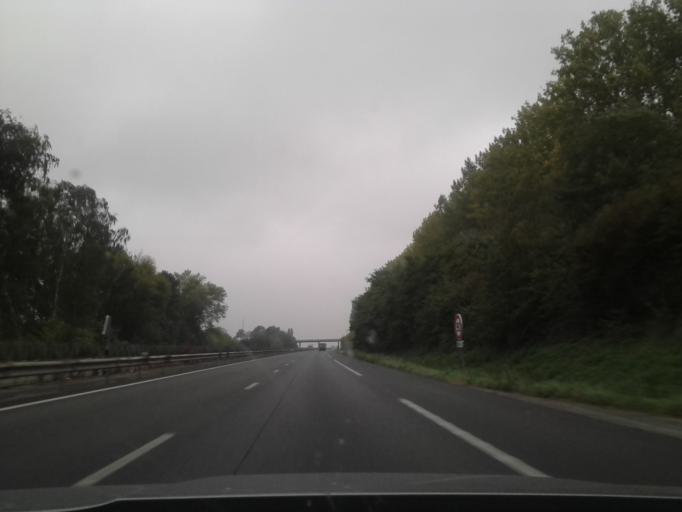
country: FR
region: Nord-Pas-de-Calais
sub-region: Departement du Nord
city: Neuville-Saint-Remy
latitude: 50.2070
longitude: 3.2263
